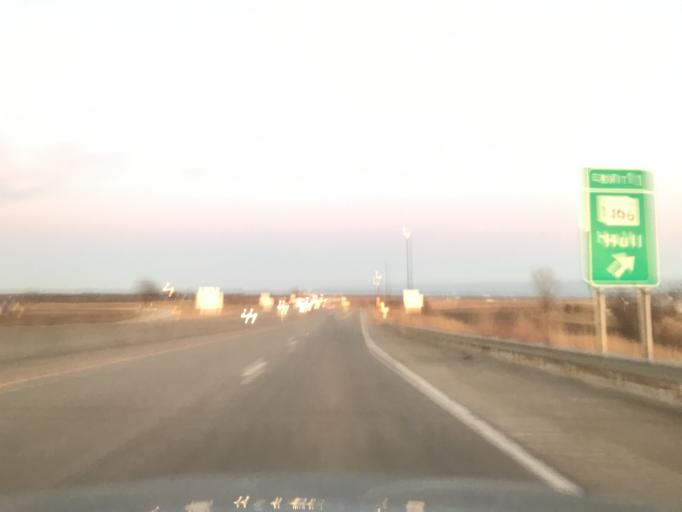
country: US
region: Missouri
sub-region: Marion County
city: Hannibal
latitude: 39.7249
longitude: -91.3444
